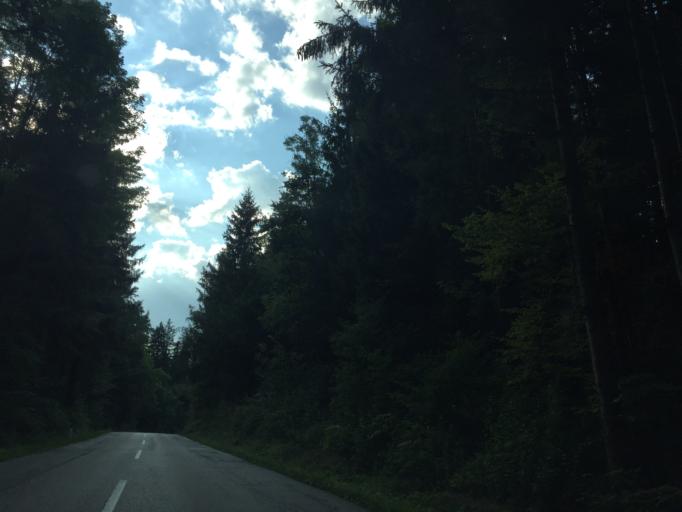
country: SI
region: Naklo
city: Naklo
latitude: 46.3016
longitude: 14.2685
